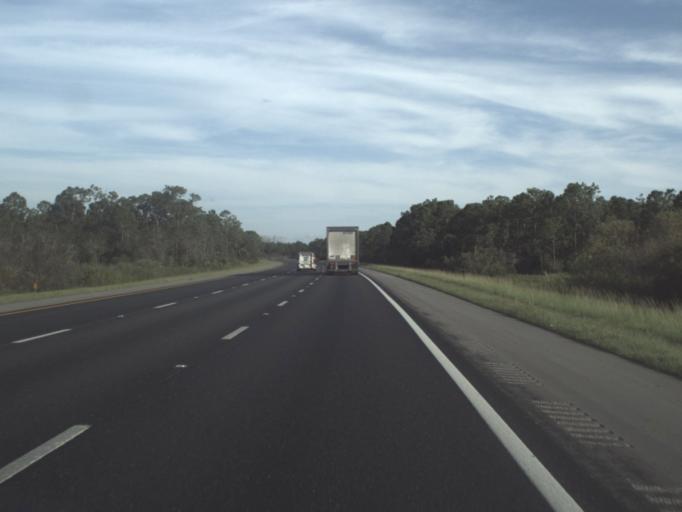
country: US
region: Florida
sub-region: Lee County
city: Suncoast Estates
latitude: 26.7822
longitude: -81.8982
